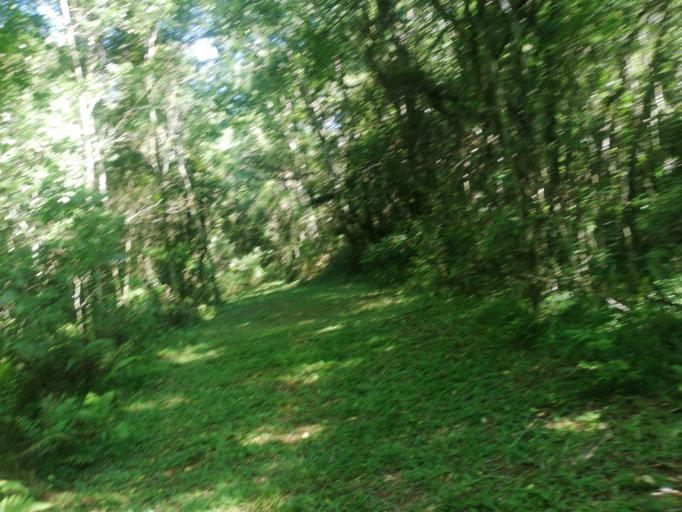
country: AR
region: Misiones
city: Cerro Azul
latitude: -27.7516
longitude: -55.5616
